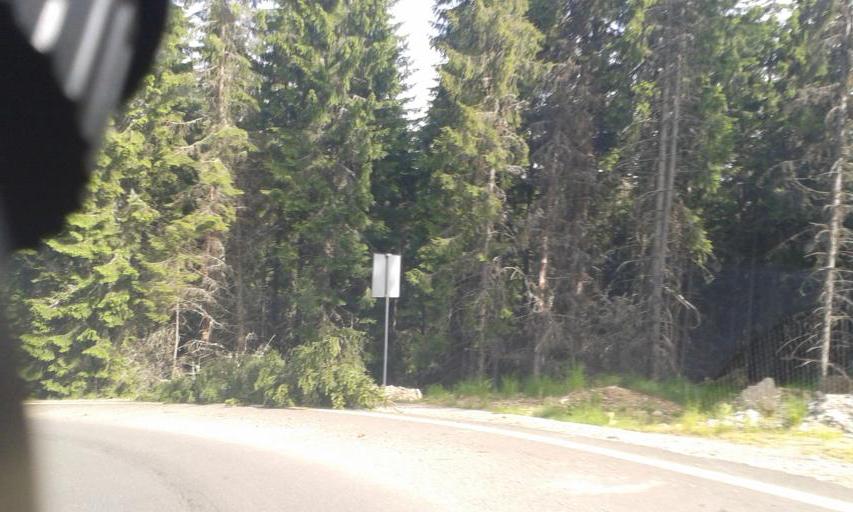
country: RO
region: Hunedoara
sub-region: Oras Petrila
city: Petrila
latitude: 45.4620
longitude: 23.6145
